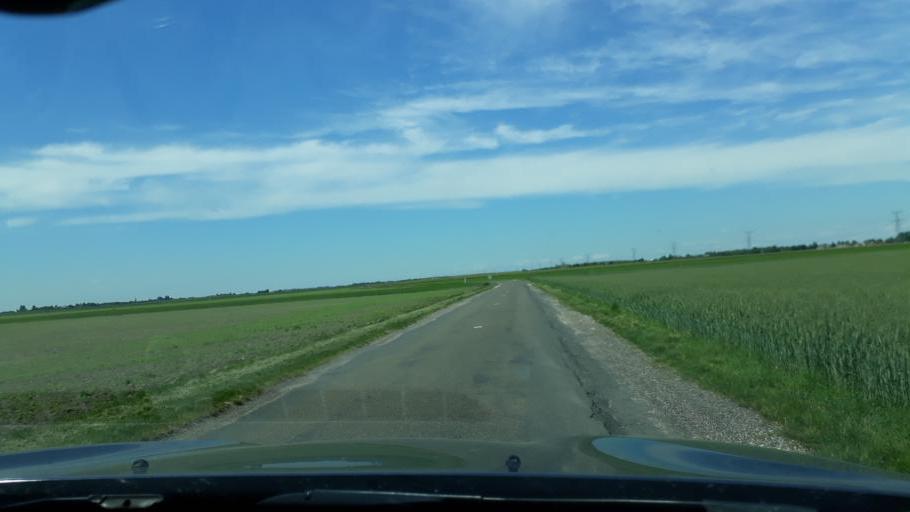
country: FR
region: Centre
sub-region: Departement du Loiret
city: Dadonville
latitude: 48.1069
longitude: 2.2392
